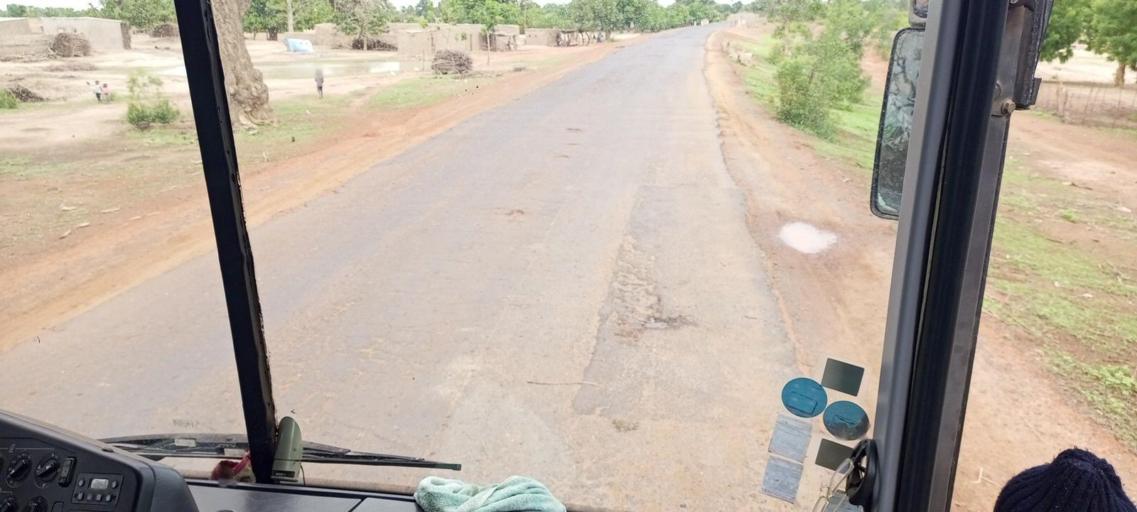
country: ML
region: Segou
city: Bla
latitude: 12.7343
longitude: -5.7259
